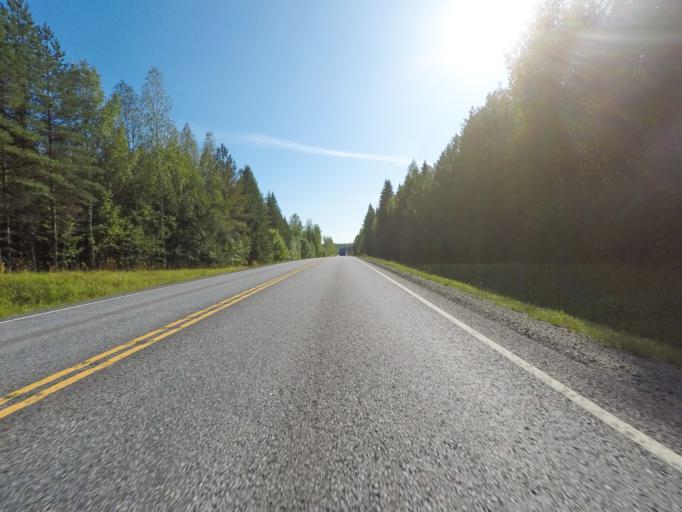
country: FI
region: Southern Savonia
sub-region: Pieksaemaeki
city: Joroinen
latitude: 62.0640
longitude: 27.8111
